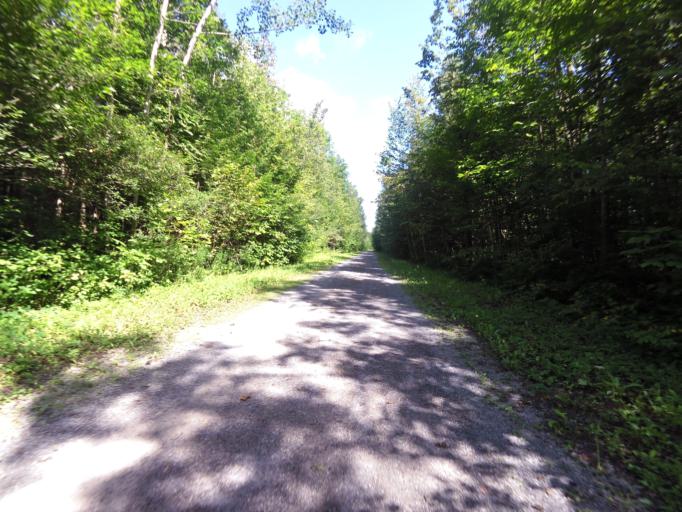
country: CA
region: Ontario
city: Ottawa
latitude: 45.2046
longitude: -75.6244
